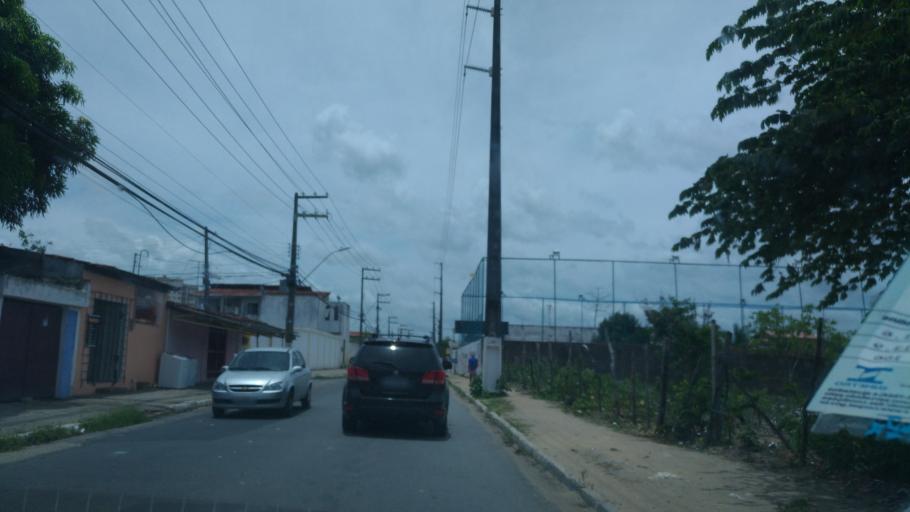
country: BR
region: Alagoas
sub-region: Satuba
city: Satuba
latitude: -9.5643
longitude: -35.7427
